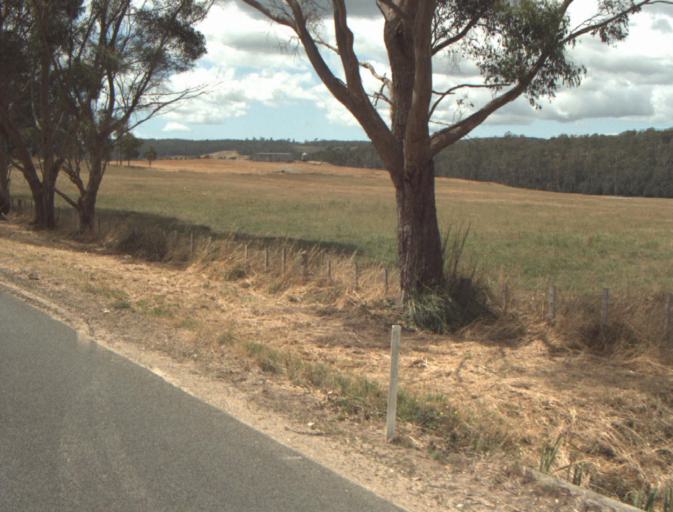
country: AU
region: Tasmania
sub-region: Launceston
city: Mayfield
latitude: -41.2230
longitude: 147.1217
